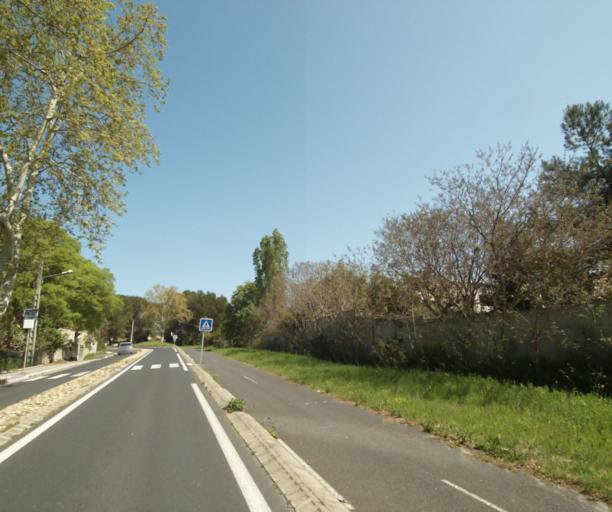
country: FR
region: Languedoc-Roussillon
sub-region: Departement de l'Herault
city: Castelnau-le-Lez
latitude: 43.6471
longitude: 3.8992
